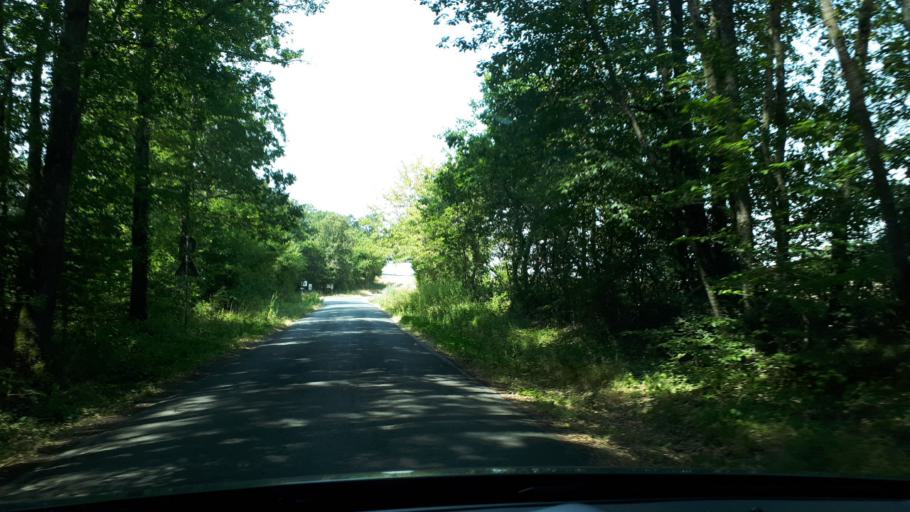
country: FR
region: Centre
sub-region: Departement du Loir-et-Cher
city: Aze
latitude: 47.8411
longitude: 1.0183
